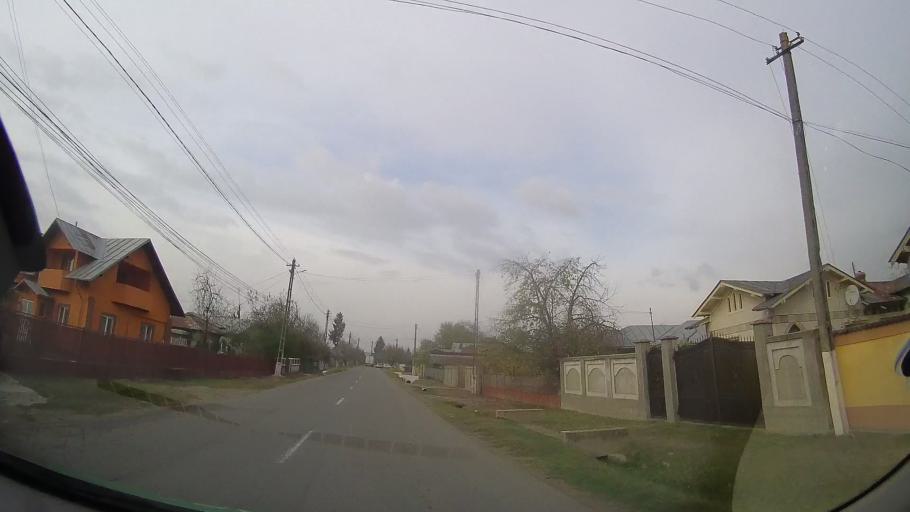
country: RO
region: Prahova
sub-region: Comuna Gorgota
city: Potigrafu
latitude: 44.7764
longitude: 26.1049
